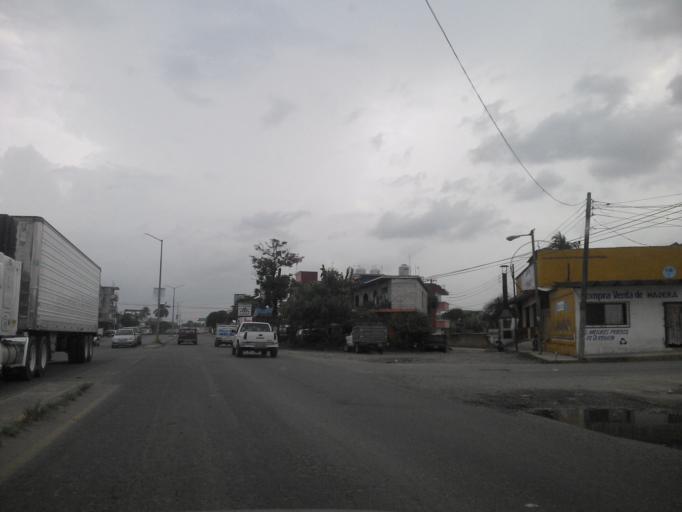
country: MX
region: Veracruz
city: Martinez de la Torre
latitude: 20.0742
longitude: -97.0624
